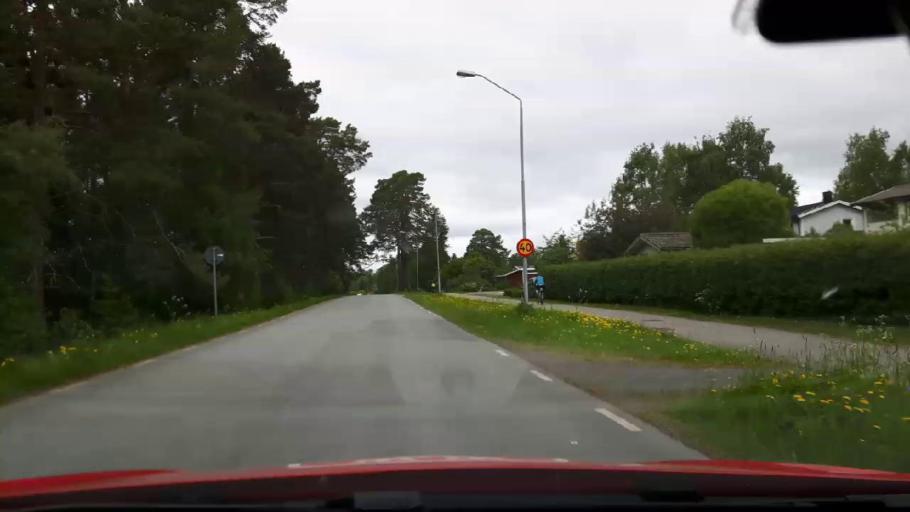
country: SE
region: Jaemtland
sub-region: OEstersunds Kommun
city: Ostersund
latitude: 63.1988
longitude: 14.6398
